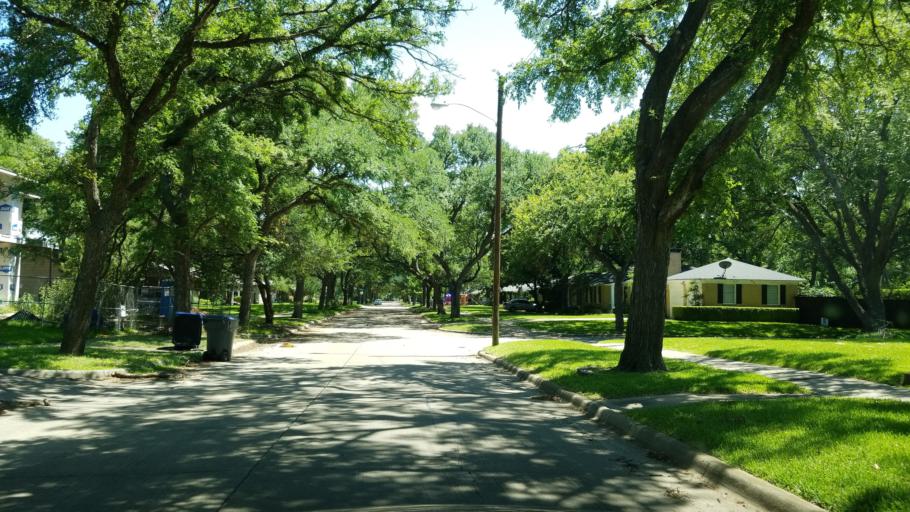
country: US
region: Texas
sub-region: Dallas County
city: University Park
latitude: 32.8761
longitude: -96.8524
